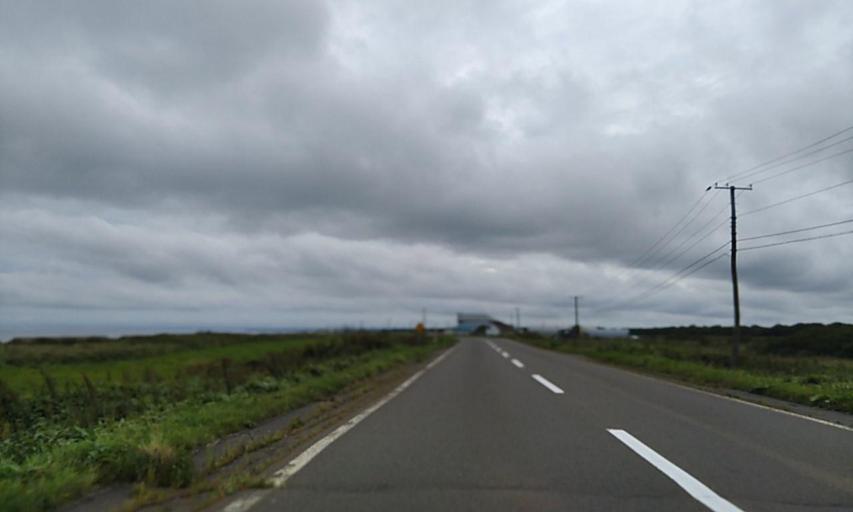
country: JP
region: Hokkaido
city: Shibetsu
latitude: 43.4178
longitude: 145.2691
